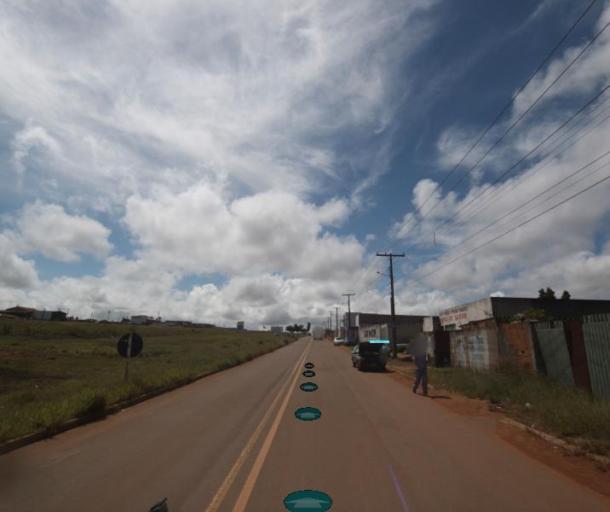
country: BR
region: Federal District
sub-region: Brasilia
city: Brasilia
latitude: -15.7385
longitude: -48.2947
